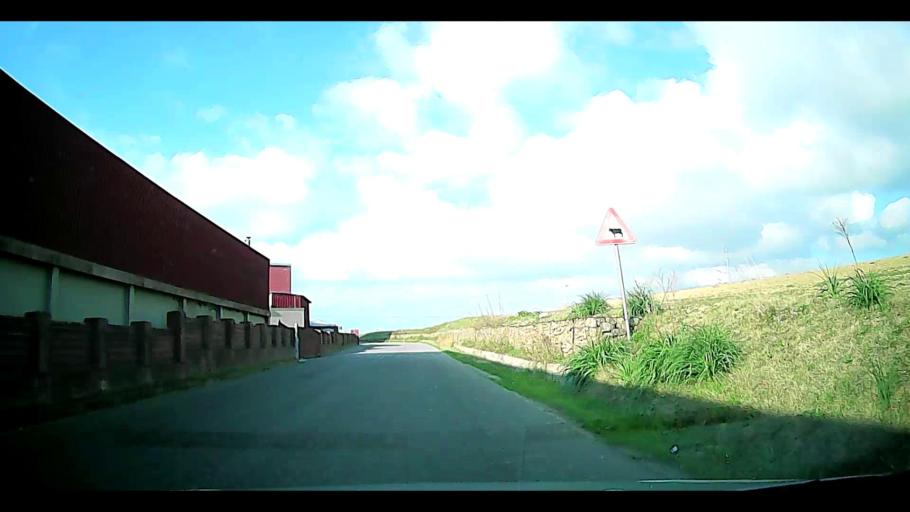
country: IT
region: Calabria
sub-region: Provincia di Crotone
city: Rocca di Neto
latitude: 39.1820
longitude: 17.0413
